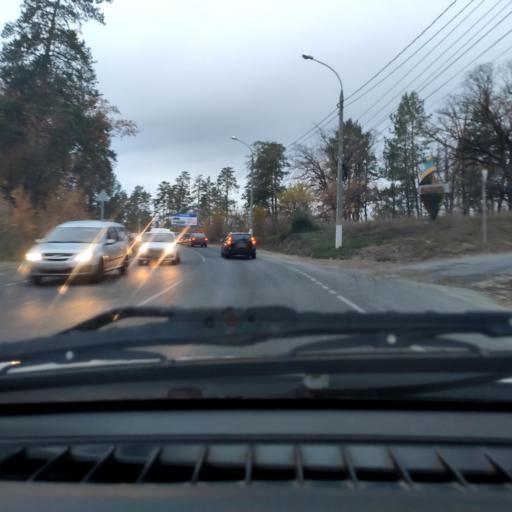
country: RU
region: Samara
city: Tol'yatti
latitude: 53.4808
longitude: 49.3223
